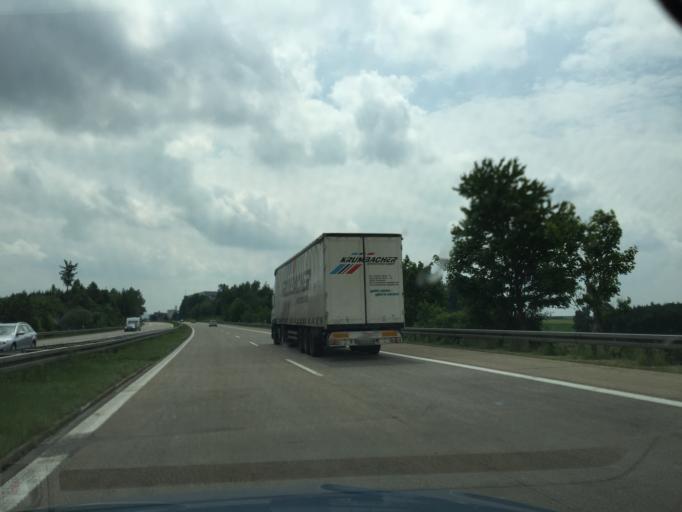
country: DE
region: Baden-Wuerttemberg
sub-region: Regierungsbezirk Stuttgart
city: Ellwangen
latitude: 48.9689
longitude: 10.1863
